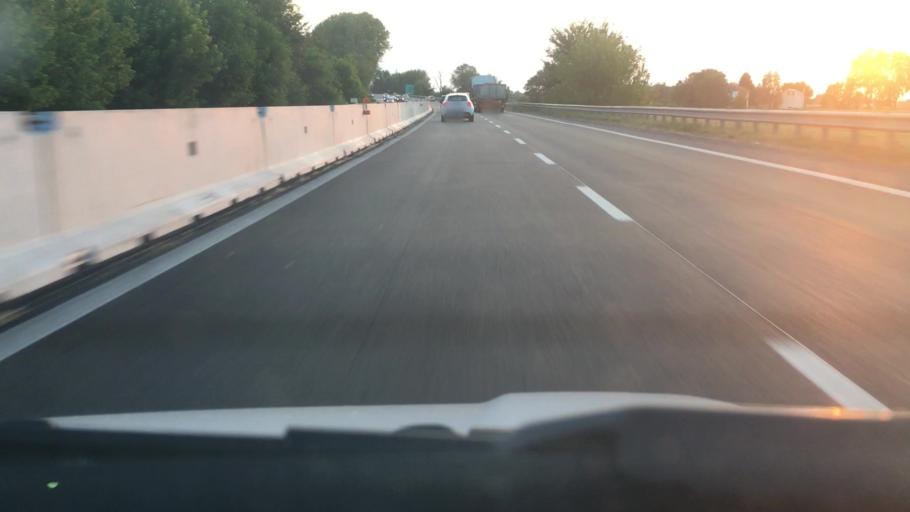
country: IT
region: Emilia-Romagna
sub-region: Provincia di Ferrara
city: Gaibanella-Sant'Edigio
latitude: 44.7987
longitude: 11.6542
